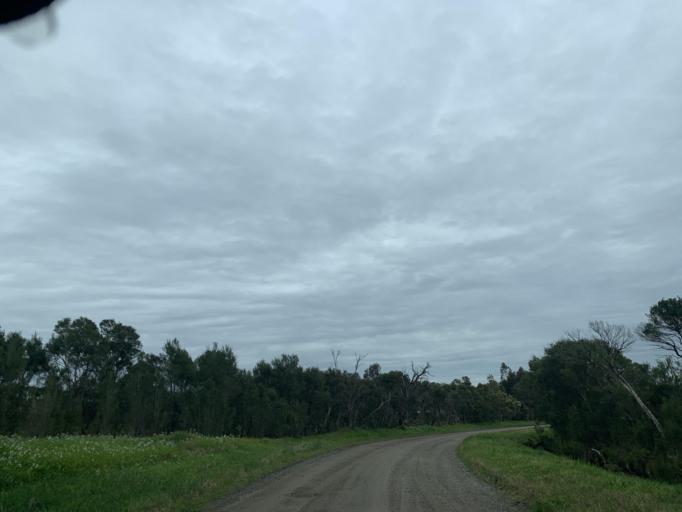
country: AU
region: Victoria
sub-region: Cardinia
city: Garfield
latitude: -38.0917
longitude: 145.6395
